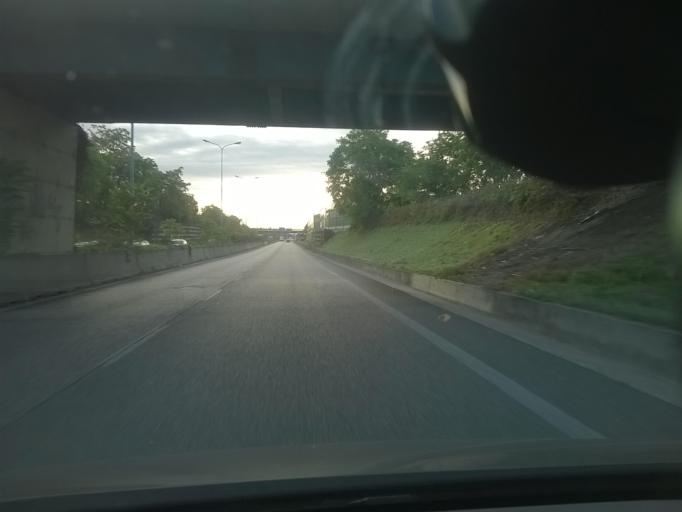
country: IT
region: Lombardy
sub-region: Provincia di Bergamo
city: Seriate
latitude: 45.6752
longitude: 9.7119
